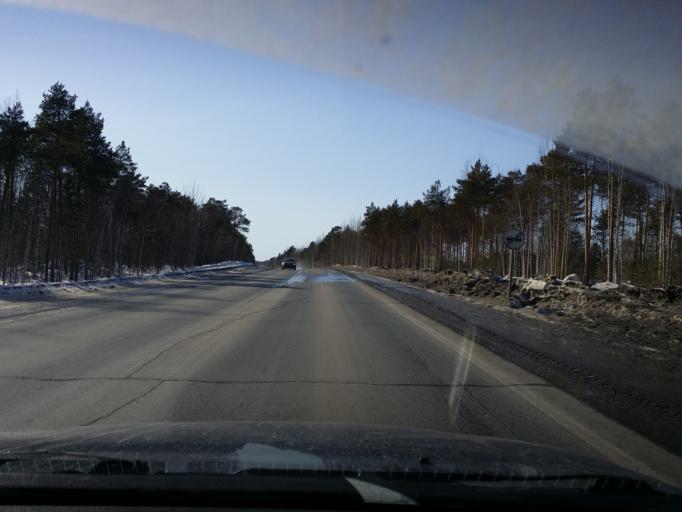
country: RU
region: Khanty-Mansiyskiy Avtonomnyy Okrug
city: Megion
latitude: 61.1633
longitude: 75.6893
